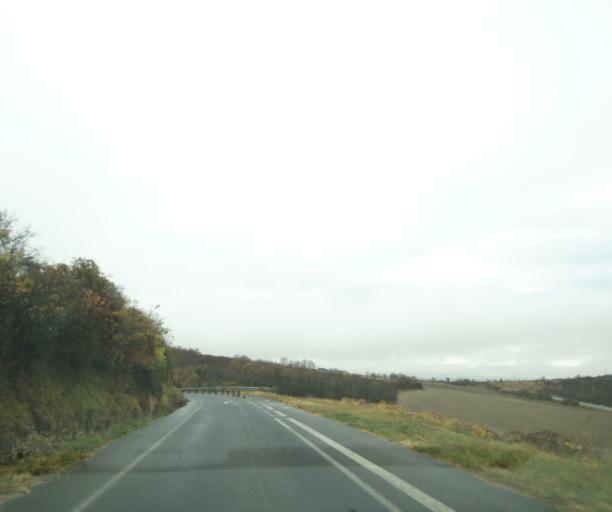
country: FR
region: Auvergne
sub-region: Departement du Puy-de-Dome
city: Cournon-d'Auvergne
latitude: 45.7557
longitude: 3.2084
